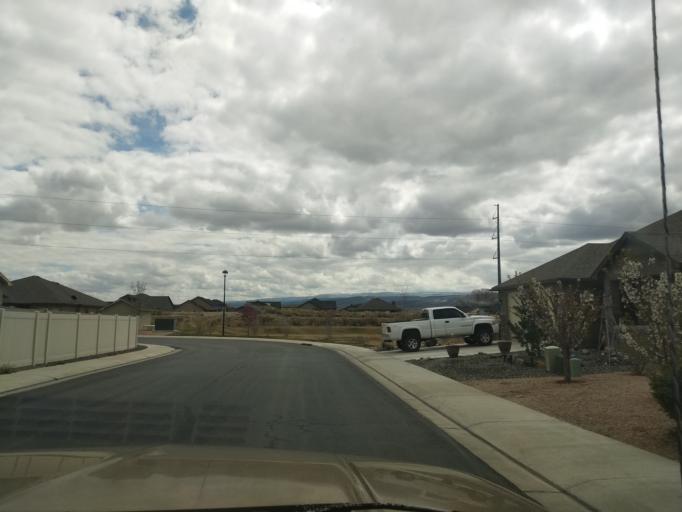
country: US
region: Colorado
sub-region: Mesa County
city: Redlands
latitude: 39.1000
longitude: -108.5937
